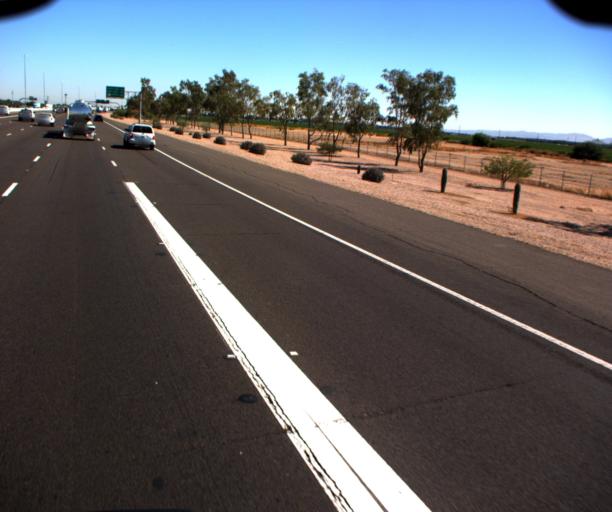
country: US
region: Arizona
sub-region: Maricopa County
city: Tolleson
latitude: 33.4600
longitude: -112.3016
